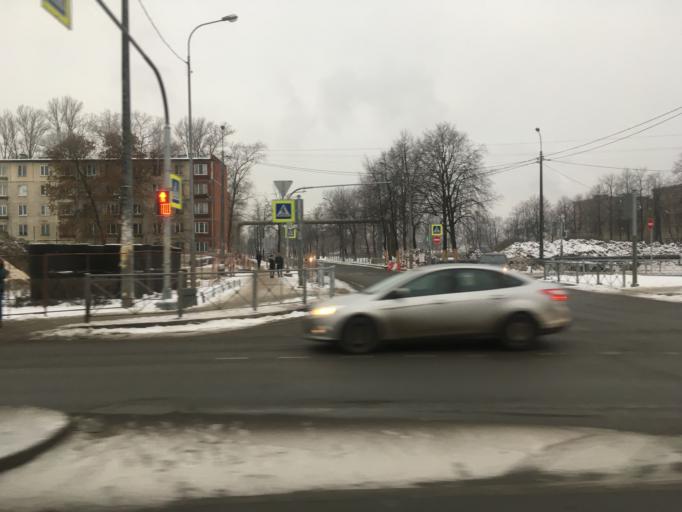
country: RU
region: St.-Petersburg
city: Obukhovo
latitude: 59.8705
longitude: 30.4402
